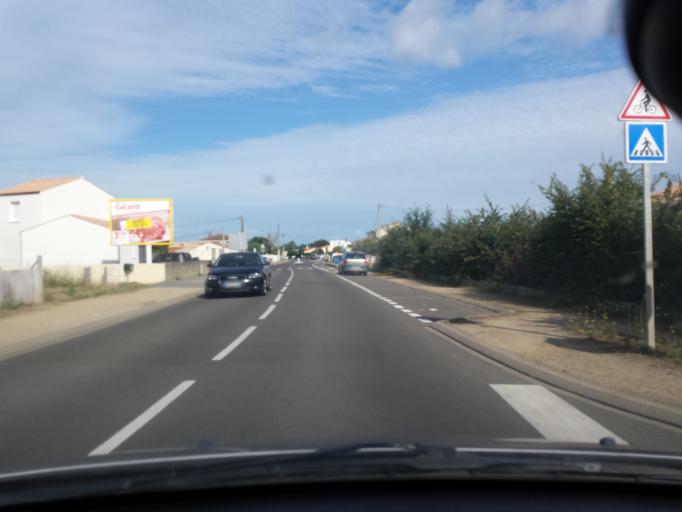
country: FR
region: Pays de la Loire
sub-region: Departement de la Vendee
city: Olonne-sur-Mer
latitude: 46.5418
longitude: -1.7967
